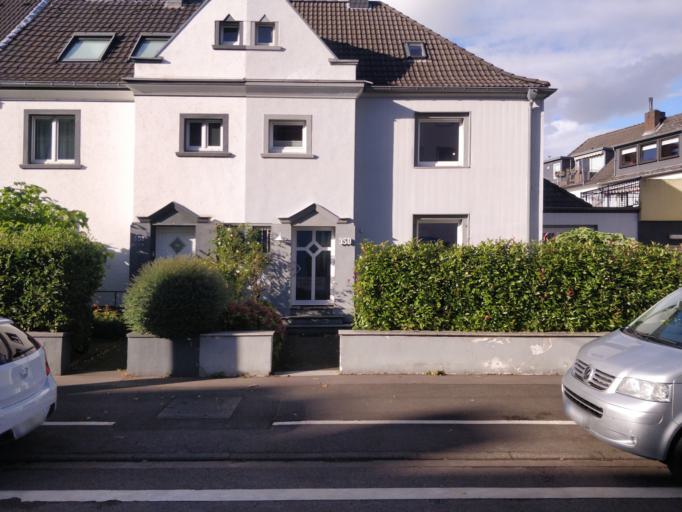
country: DE
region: North Rhine-Westphalia
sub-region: Regierungsbezirk Koln
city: Neustadt/Sued
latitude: 50.9201
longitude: 6.9135
